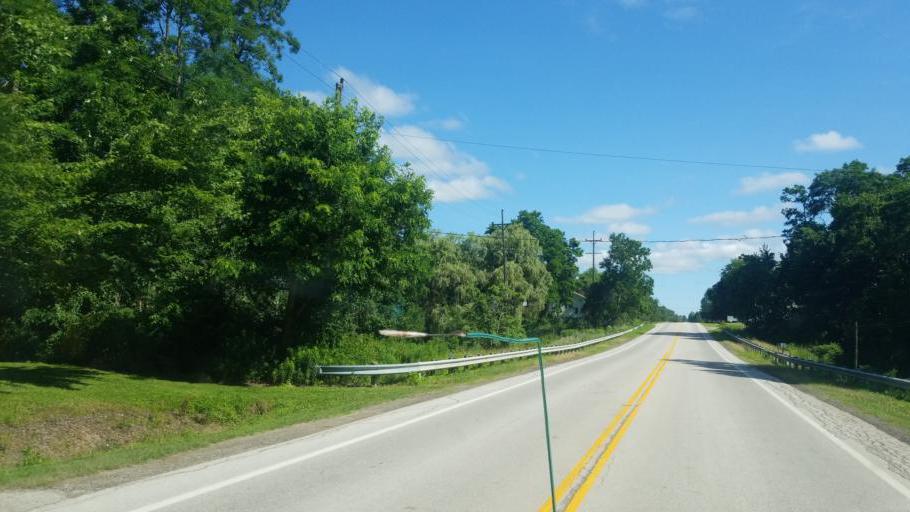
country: US
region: Ohio
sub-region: Ashtabula County
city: Conneaut
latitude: 41.8094
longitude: -80.5722
